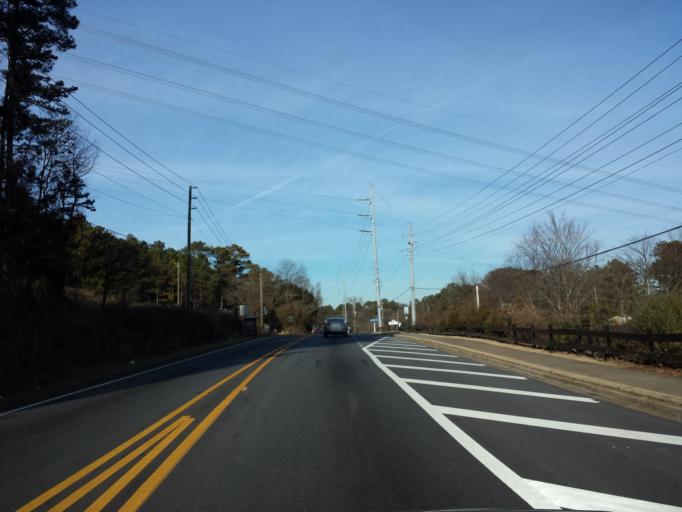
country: US
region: Georgia
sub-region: Cobb County
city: Marietta
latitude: 33.9963
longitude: -84.5480
